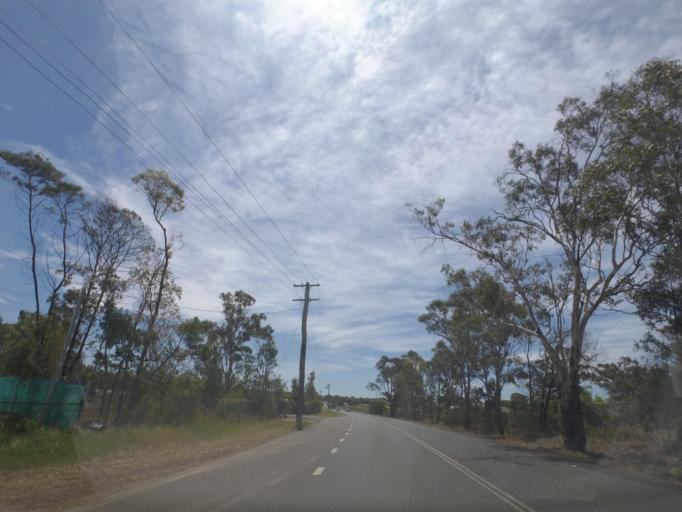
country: AU
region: New South Wales
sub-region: Wollondilly
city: Buxton
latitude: -34.2986
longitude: 150.5864
